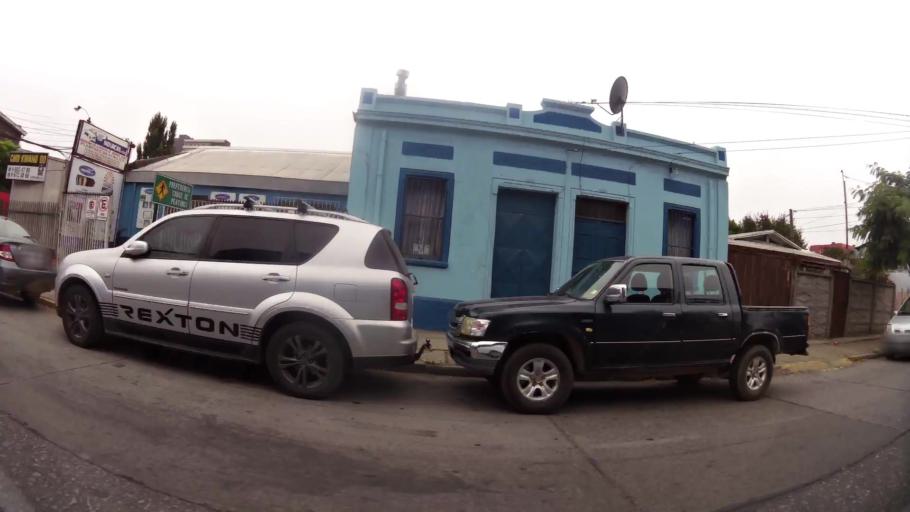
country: CL
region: Biobio
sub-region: Provincia de Concepcion
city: Concepcion
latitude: -36.8166
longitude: -73.0510
